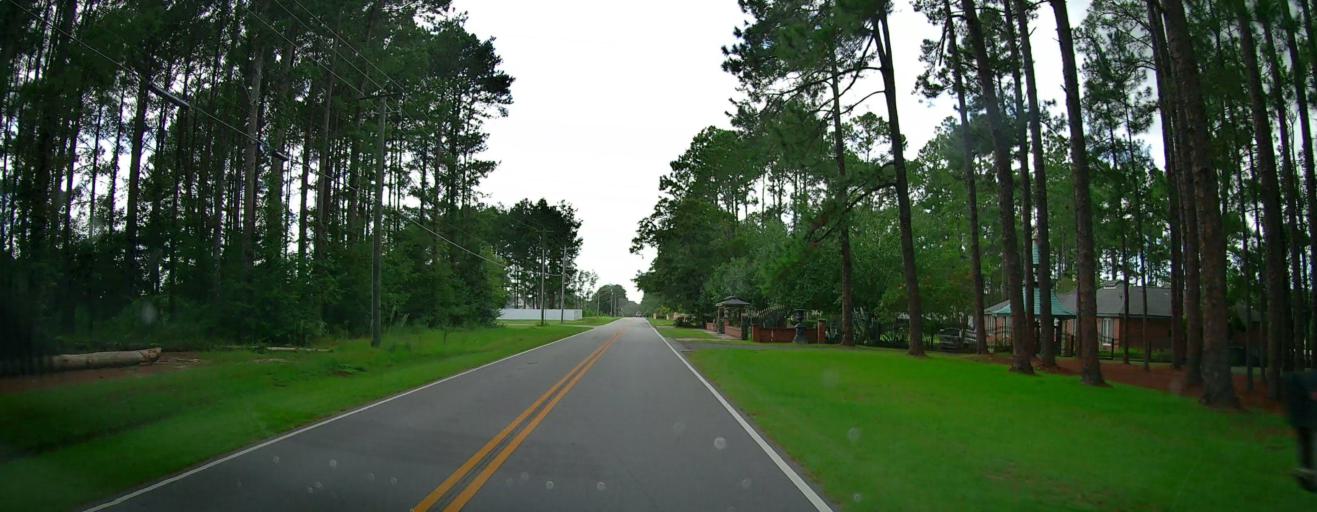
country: US
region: Georgia
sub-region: Ben Hill County
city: Fitzgerald
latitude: 31.7056
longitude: -83.2862
